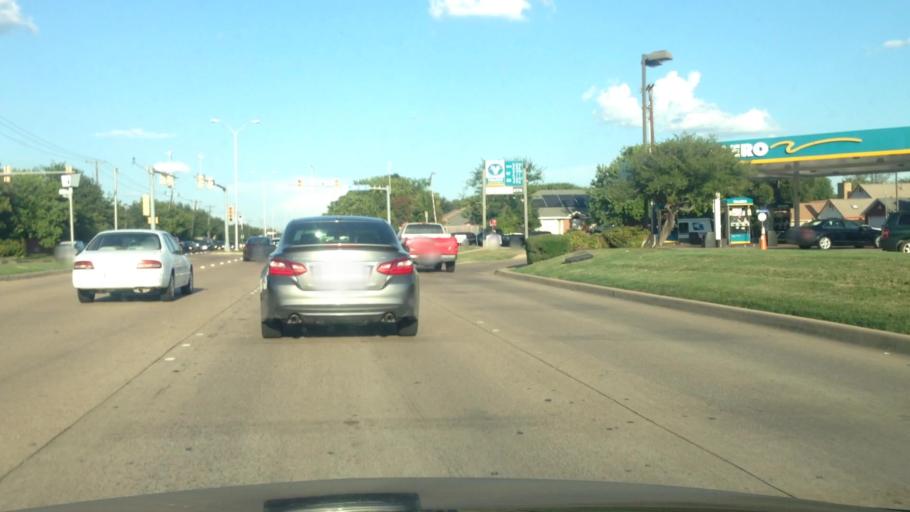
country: US
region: Texas
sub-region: Tarrant County
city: Watauga
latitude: 32.8609
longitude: -97.2862
